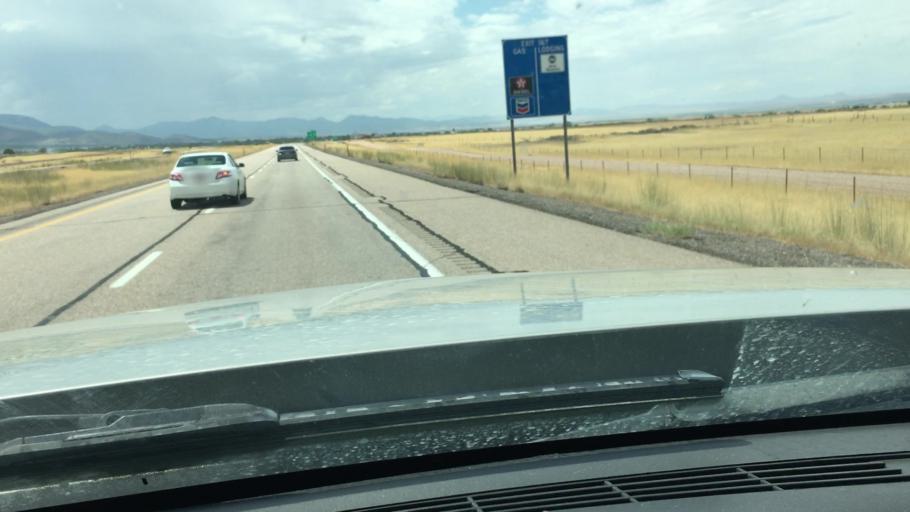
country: US
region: Utah
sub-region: Millard County
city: Fillmore
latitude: 39.0122
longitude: -112.3088
